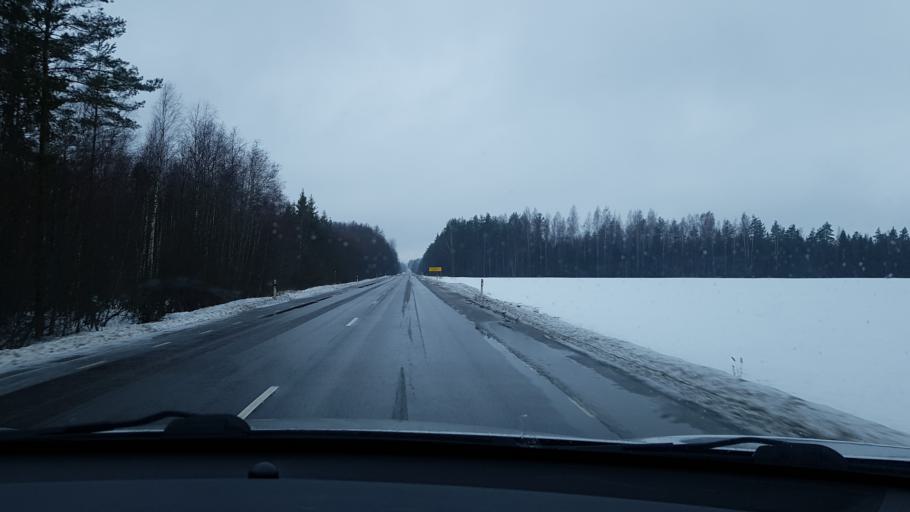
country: EE
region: Jaervamaa
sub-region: Tueri vald
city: Sarevere
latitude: 58.8056
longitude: 25.2129
